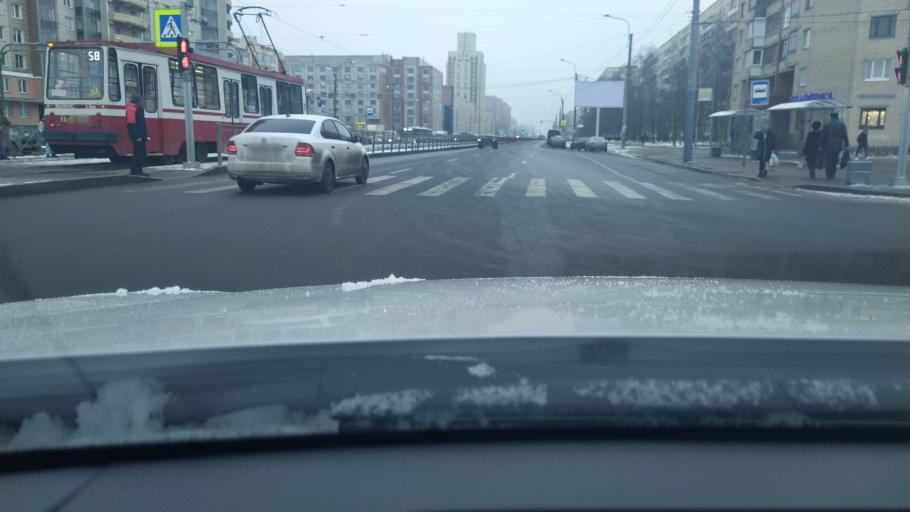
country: RU
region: Leningrad
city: Murino
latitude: 60.0334
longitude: 30.4312
